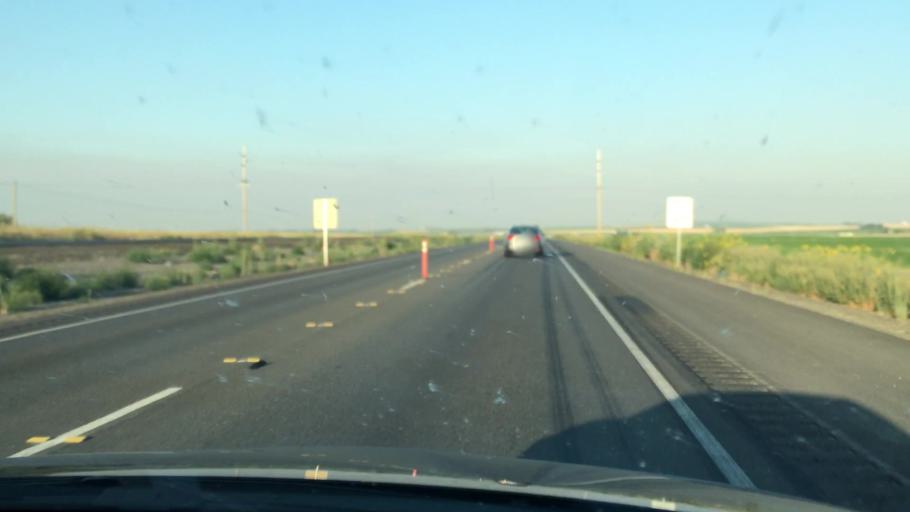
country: US
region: Idaho
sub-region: Twin Falls County
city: Hansen
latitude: 42.5760
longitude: -114.2332
